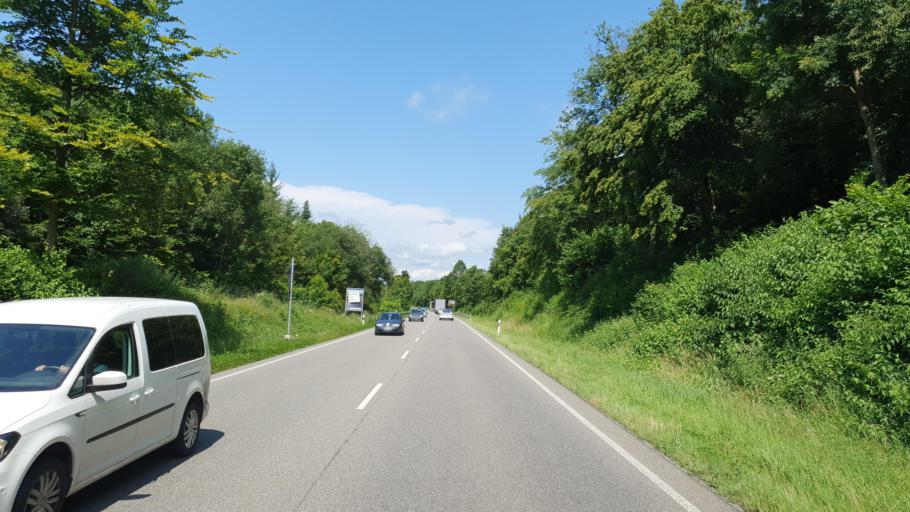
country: DE
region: Baden-Wuerttemberg
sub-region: Tuebingen Region
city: Daisendorf
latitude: 47.7093
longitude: 9.2598
